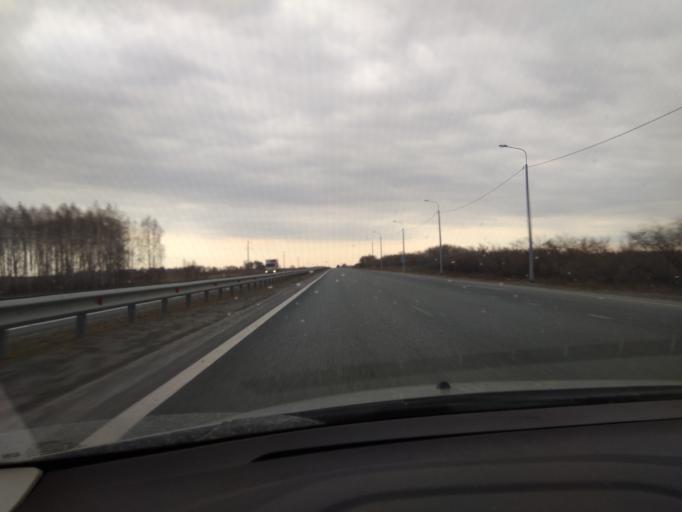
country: RU
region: Chelyabinsk
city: Kunashak
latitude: 55.7457
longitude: 61.2269
